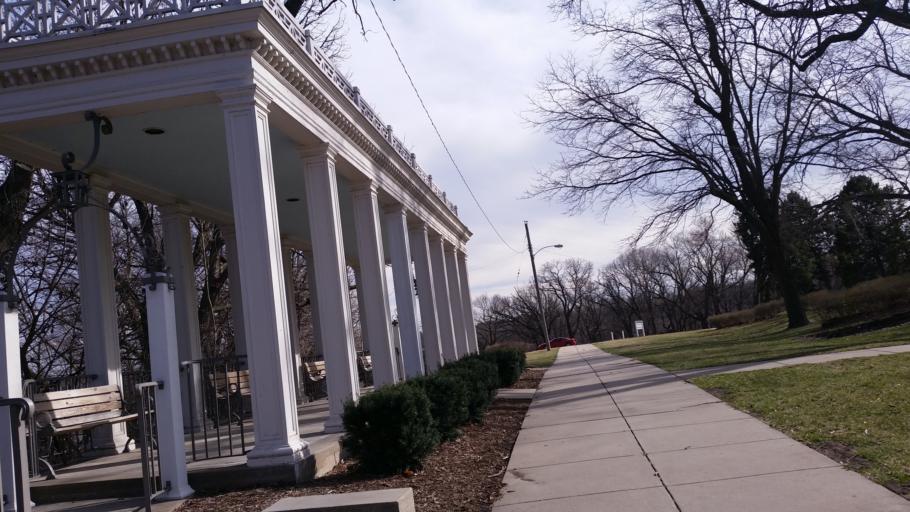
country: US
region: Nebraska
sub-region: Douglas County
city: Omaha
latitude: 41.1997
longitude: -95.9323
